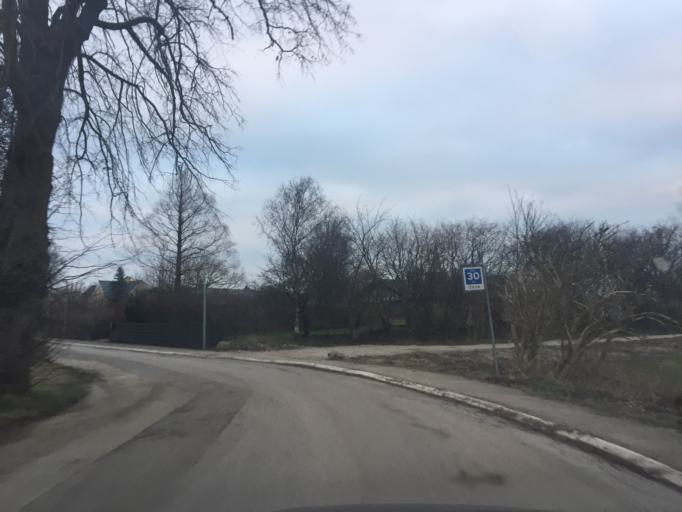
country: DK
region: Capital Region
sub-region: Halsnaes Kommune
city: Frederiksvaerk
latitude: 55.9839
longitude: 12.0327
